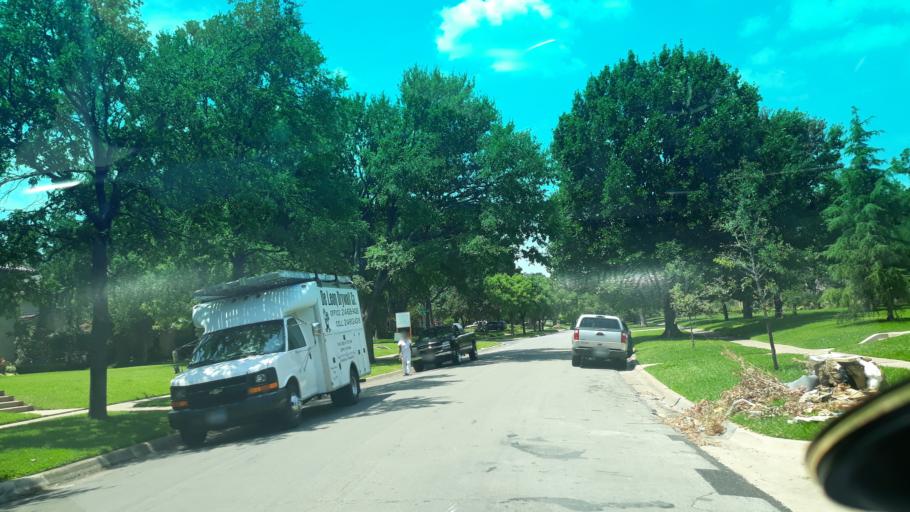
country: US
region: Texas
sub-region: Dallas County
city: Highland Park
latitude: 32.8222
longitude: -96.7353
